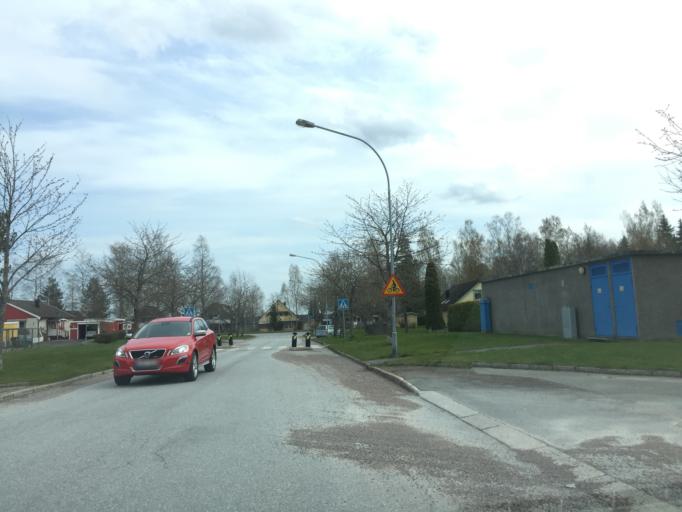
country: SE
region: OErebro
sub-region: Orebro Kommun
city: Orebro
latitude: 59.3126
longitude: 15.1815
